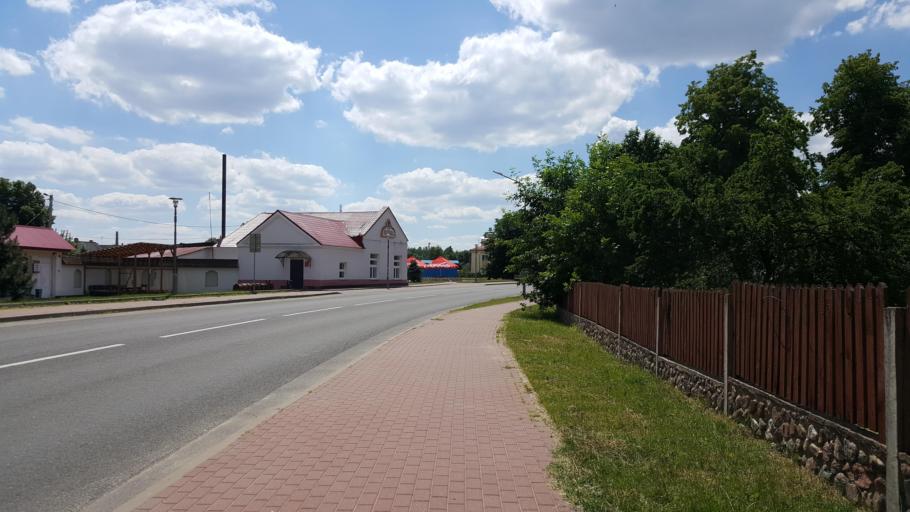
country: BY
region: Brest
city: Kamyanyuki
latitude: 52.5625
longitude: 23.8000
